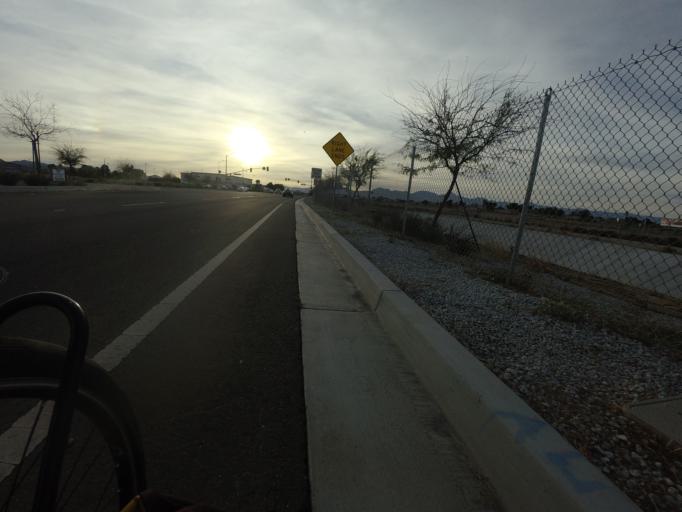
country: US
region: California
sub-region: Kern County
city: Ridgecrest
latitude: 35.6079
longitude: -117.6692
